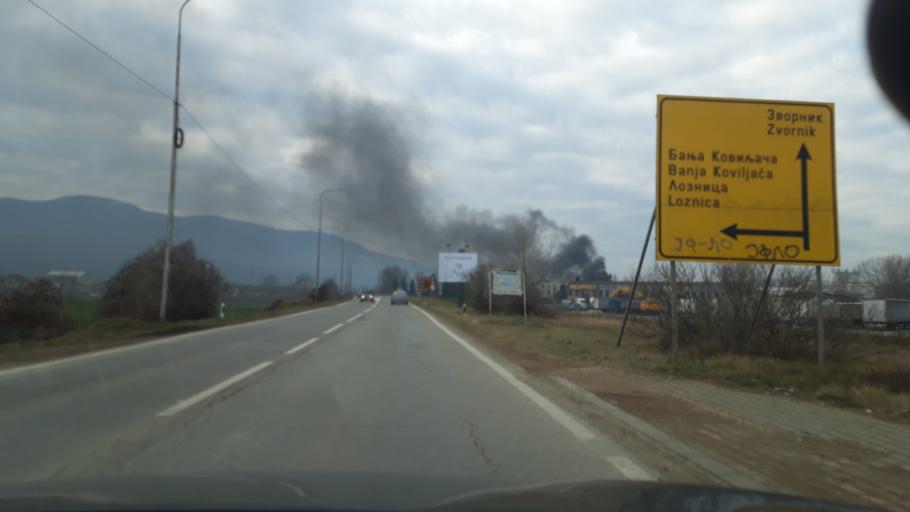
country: RS
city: Trsic
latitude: 44.5383
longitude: 19.1844
